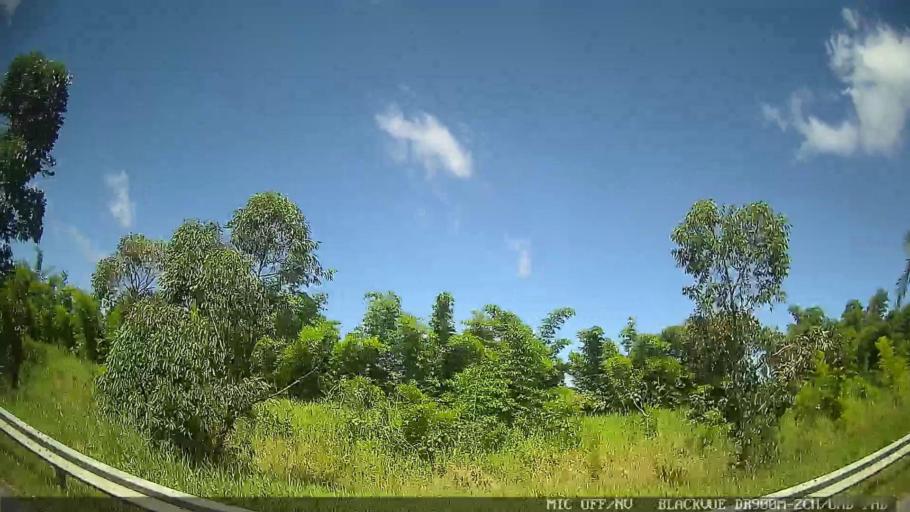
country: BR
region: Sao Paulo
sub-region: Suzano
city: Suzano
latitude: -23.5651
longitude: -46.2558
